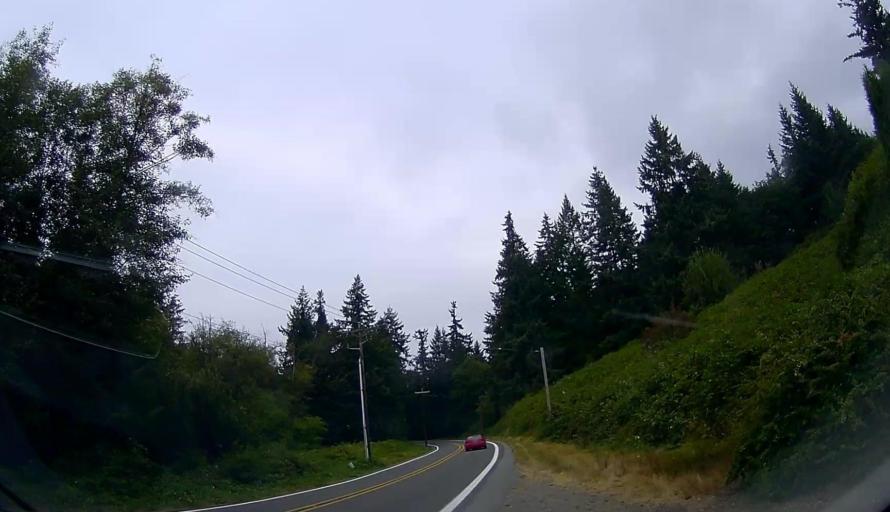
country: US
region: Washington
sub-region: Snohomish County
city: Warm Beach
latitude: 48.1426
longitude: -122.3574
